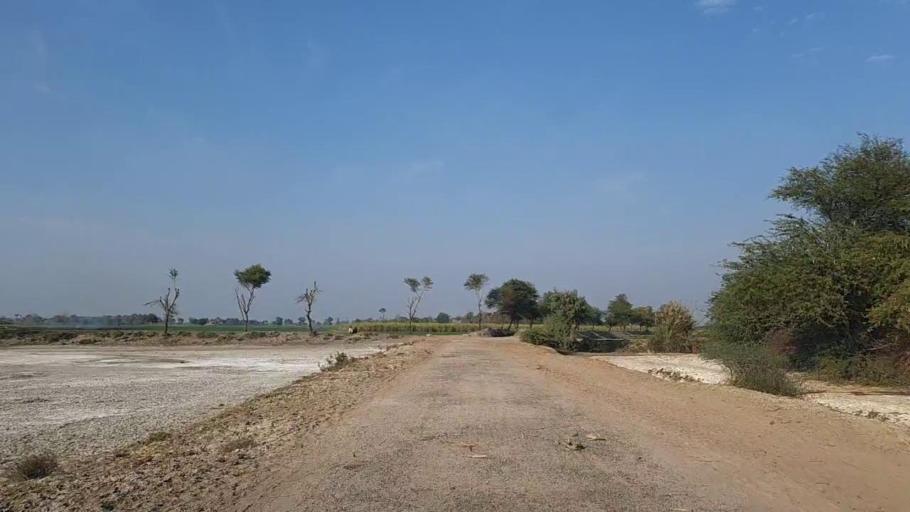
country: PK
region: Sindh
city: Nawabshah
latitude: 26.3698
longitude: 68.4910
